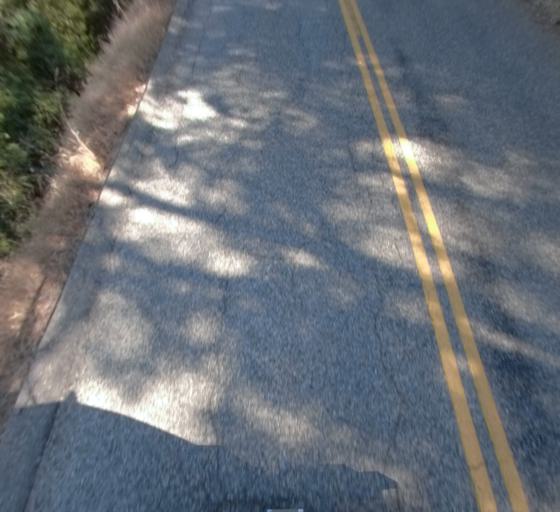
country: US
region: California
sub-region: Fresno County
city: Auberry
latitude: 37.1837
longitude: -119.4305
